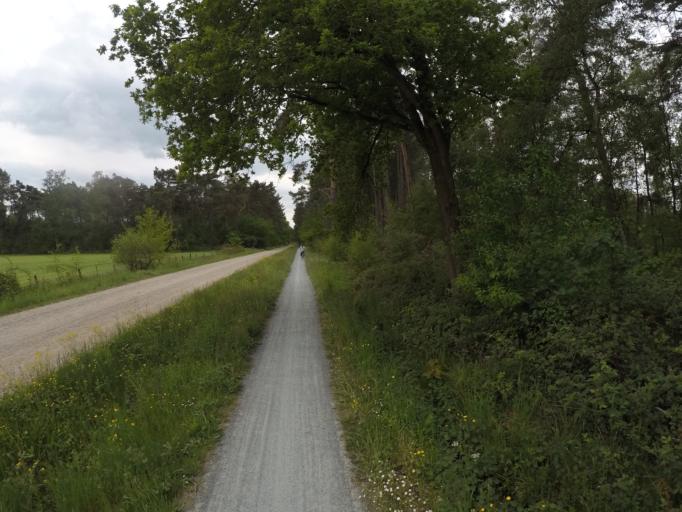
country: BE
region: Flanders
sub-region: Provincie Antwerpen
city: Oostmalle
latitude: 51.2830
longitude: 4.7420
